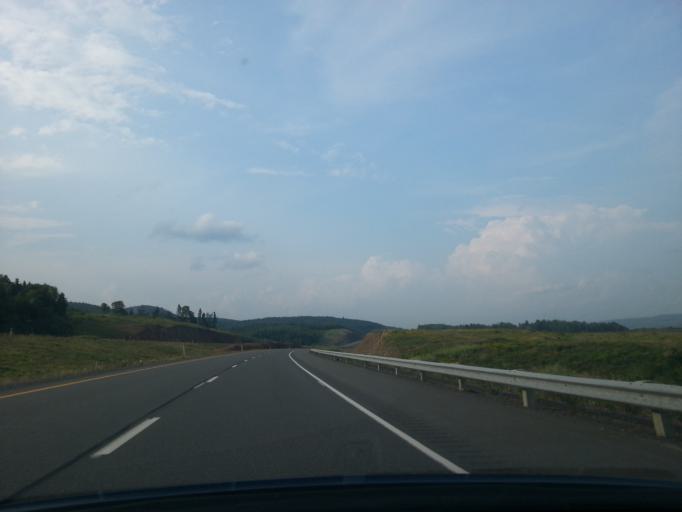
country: US
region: Maine
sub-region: Aroostook County
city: Fort Fairfield
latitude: 46.6980
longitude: -67.7398
